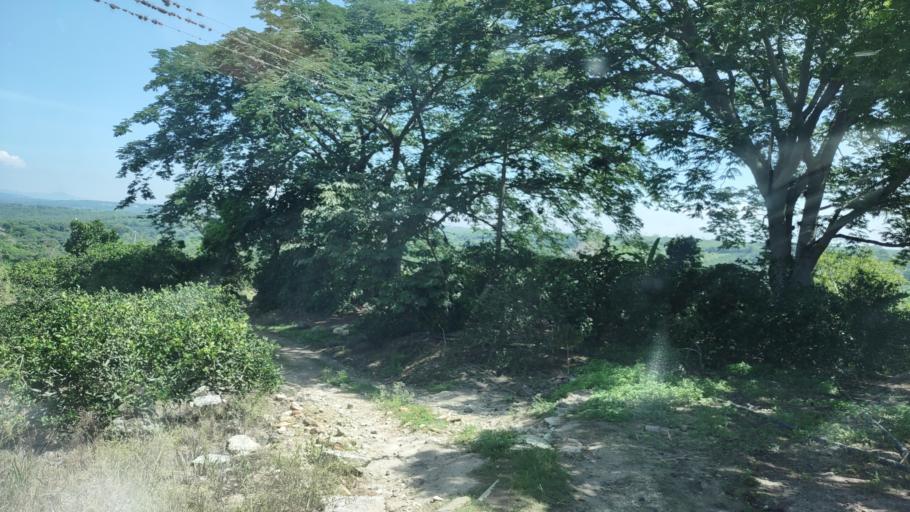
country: MX
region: Veracruz
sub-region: Emiliano Zapata
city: Dos Rios
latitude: 19.4298
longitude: -96.7938
